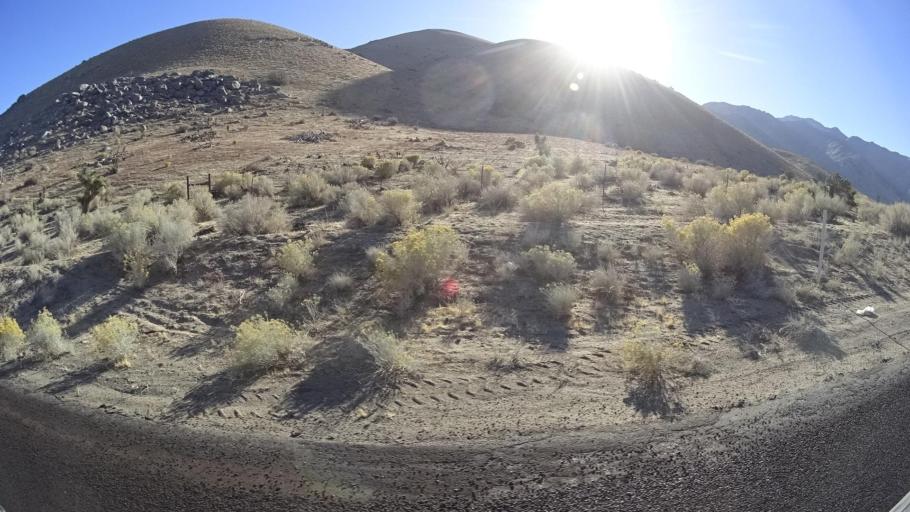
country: US
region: California
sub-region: Kern County
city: Weldon
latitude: 35.6165
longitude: -118.2530
